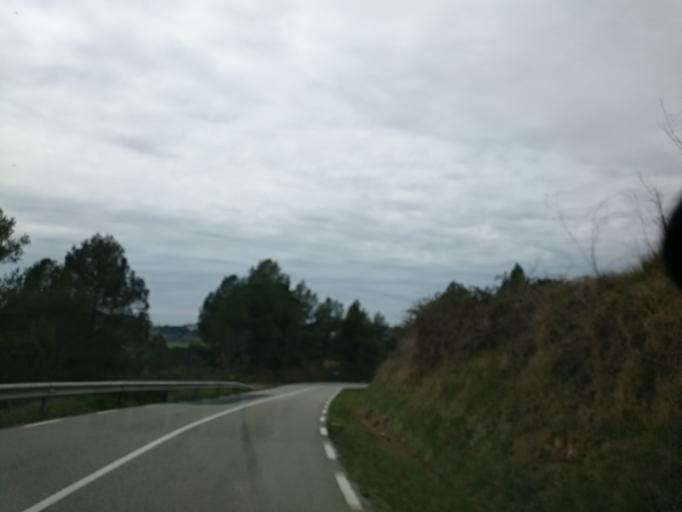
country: ES
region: Catalonia
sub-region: Provincia de Barcelona
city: Sant Sadurni d'Anoia
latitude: 41.4413
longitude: 1.8011
